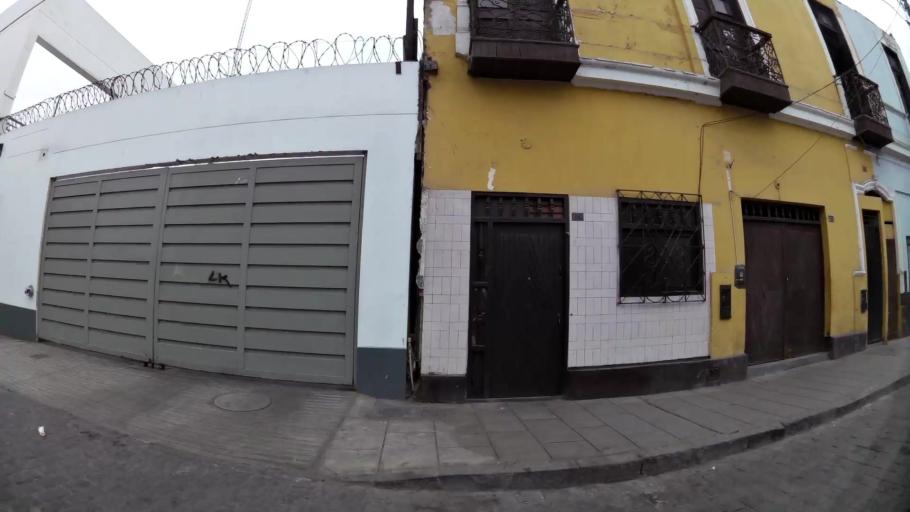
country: PE
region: Callao
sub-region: Callao
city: Callao
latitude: -12.0603
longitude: -77.1436
